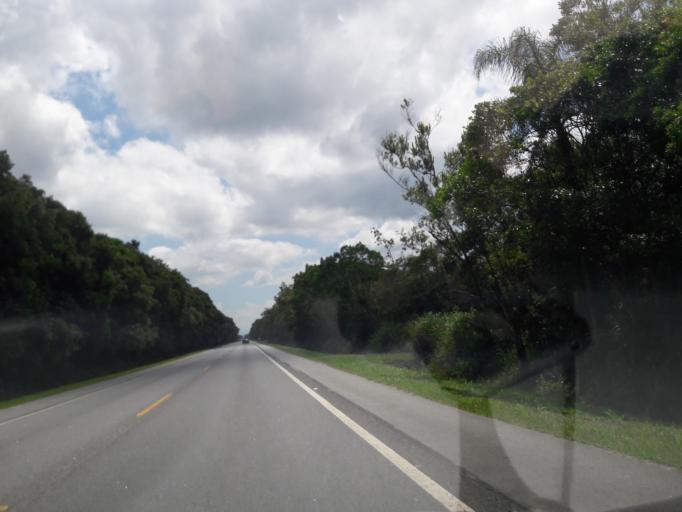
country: BR
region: Parana
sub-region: Pontal Do Parana
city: Pontal do Parana
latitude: -25.6256
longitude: -48.5424
